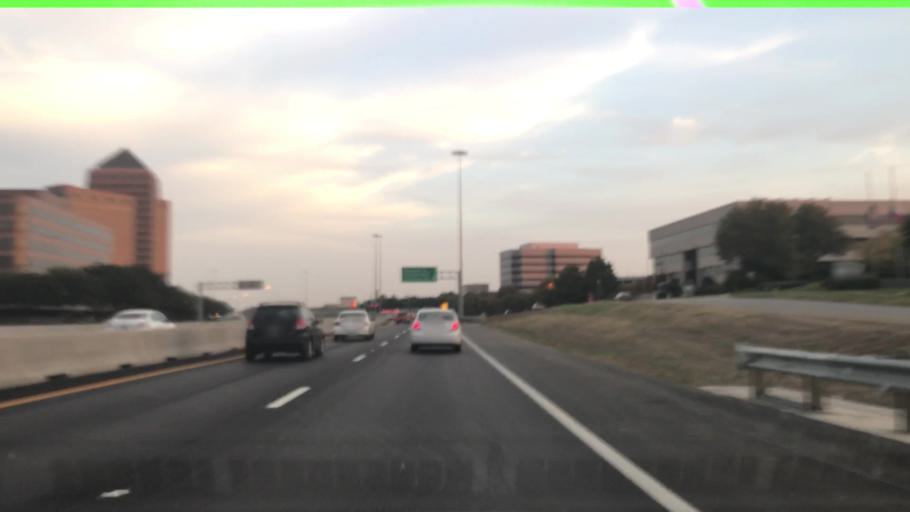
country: US
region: Texas
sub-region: Dallas County
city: Irving
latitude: 32.8614
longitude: -96.9372
